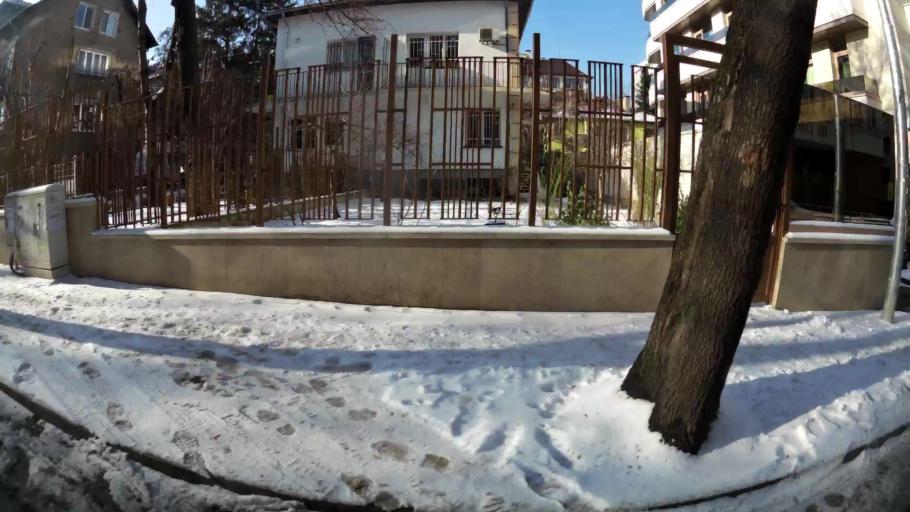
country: BG
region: Sofia-Capital
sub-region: Stolichna Obshtina
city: Sofia
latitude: 42.6752
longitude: 23.3543
